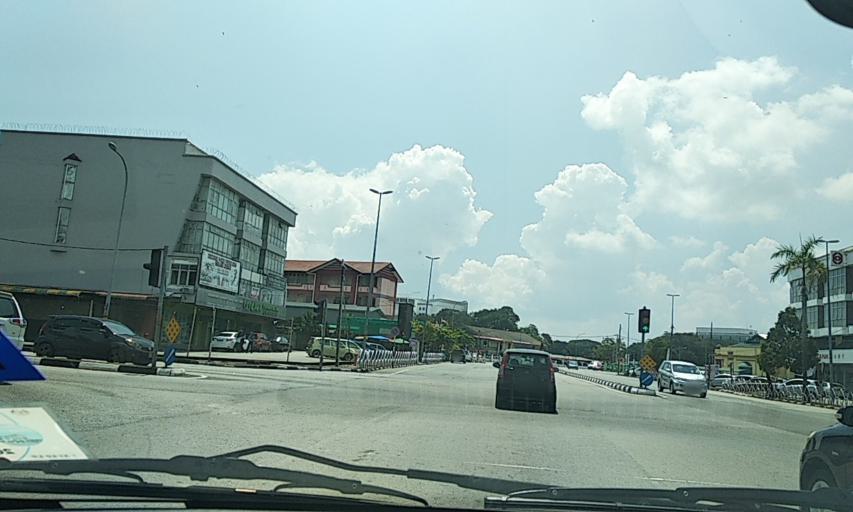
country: MY
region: Kedah
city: Sungai Petani
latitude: 5.6404
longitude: 100.4837
